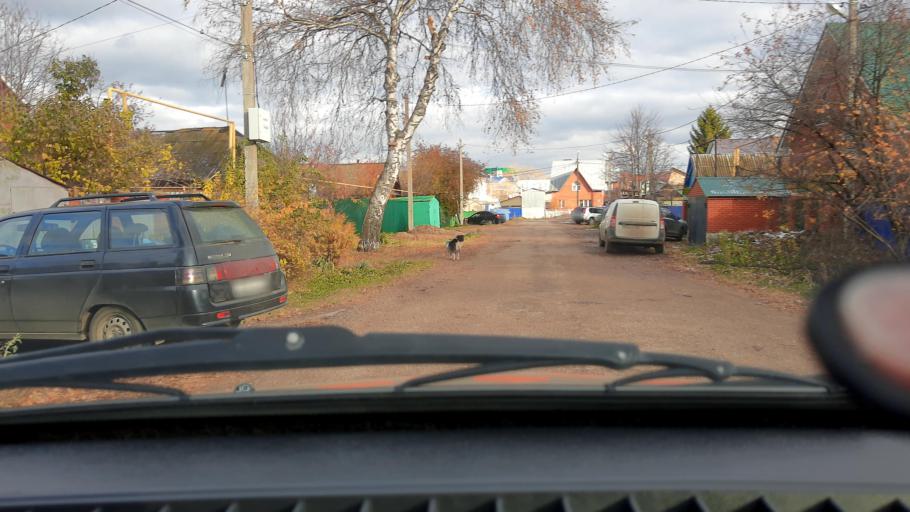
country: RU
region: Bashkortostan
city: Ufa
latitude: 54.7791
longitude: 56.0626
